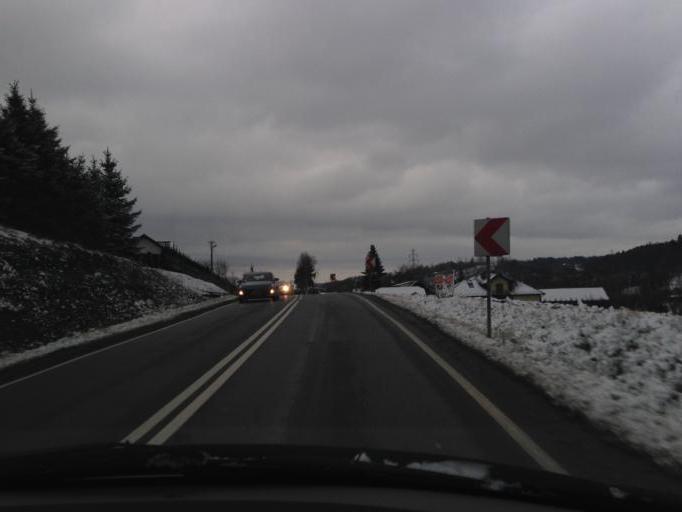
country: PL
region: Lesser Poland Voivodeship
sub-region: Powiat tarnowski
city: Siemiechow
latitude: 49.8544
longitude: 20.8889
